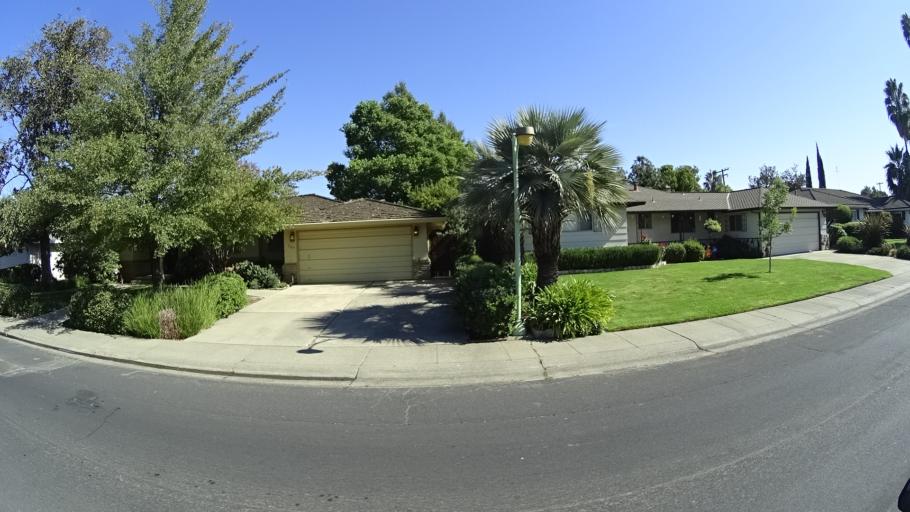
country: US
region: California
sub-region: Sacramento County
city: Parkway
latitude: 38.4912
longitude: -121.5112
